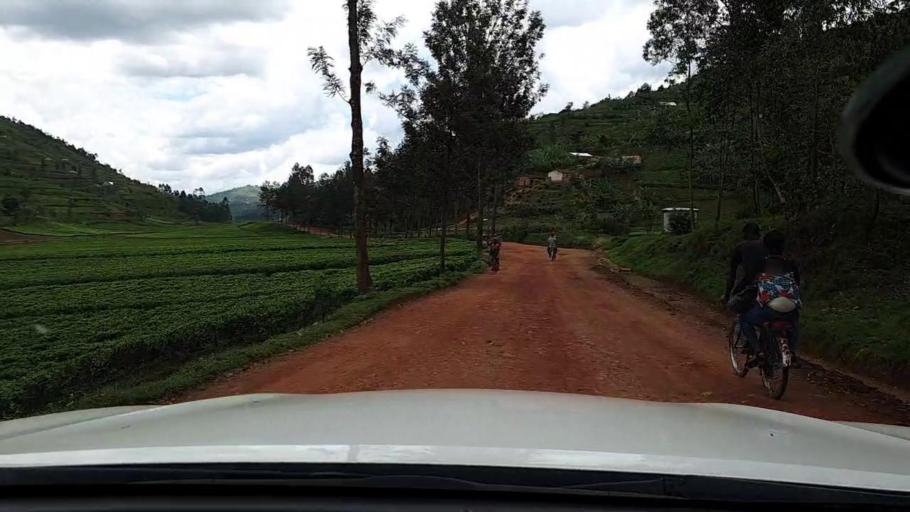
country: RW
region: Northern Province
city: Byumba
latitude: -1.6587
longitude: 29.9123
